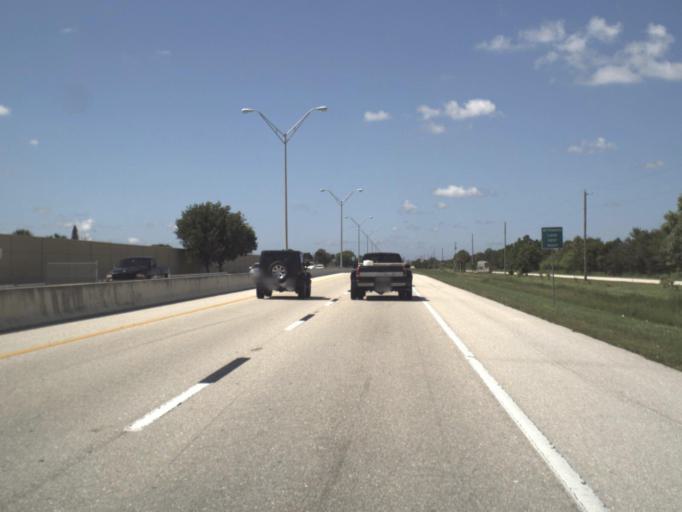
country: US
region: Florida
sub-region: Lee County
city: Lochmoor Waterway Estates
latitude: 26.6080
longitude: -81.9188
